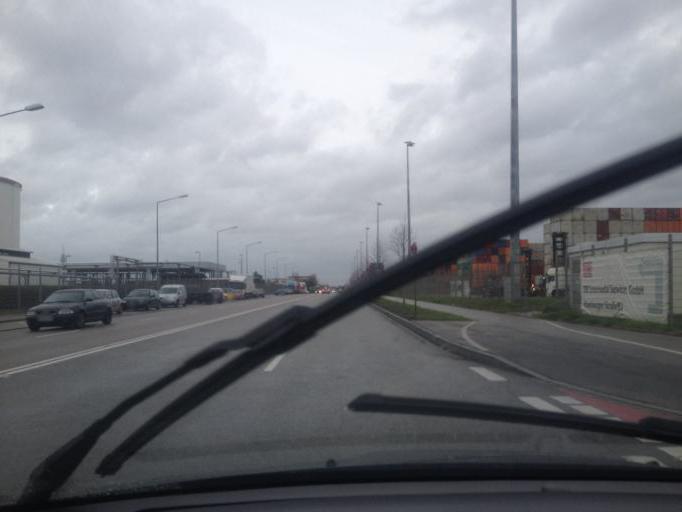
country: DE
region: Bavaria
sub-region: Regierungsbezirk Mittelfranken
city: Stein
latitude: 49.3918
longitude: 11.0502
